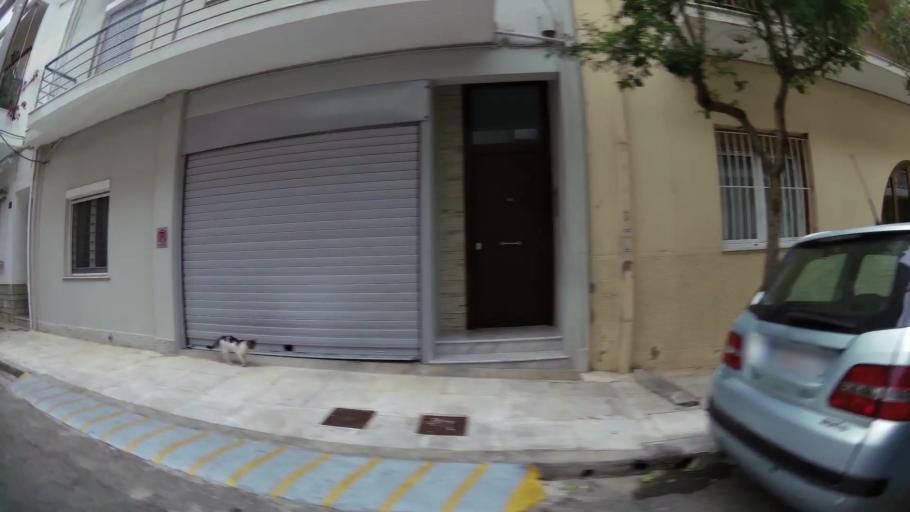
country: GR
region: Attica
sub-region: Nomarchia Athinas
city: Agia Varvara
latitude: 37.9962
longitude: 23.6725
